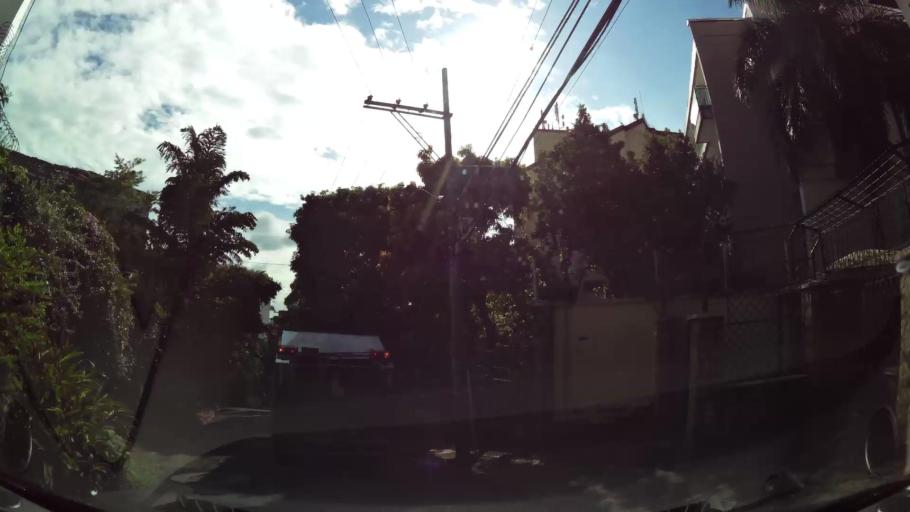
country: CO
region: Valle del Cauca
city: Cali
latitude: 3.4569
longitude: -76.5375
